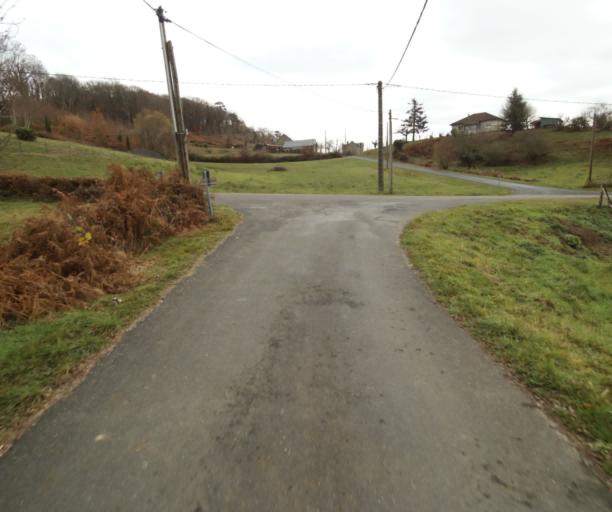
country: FR
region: Limousin
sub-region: Departement de la Correze
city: Saint-Mexant
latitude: 45.2876
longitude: 1.6337
